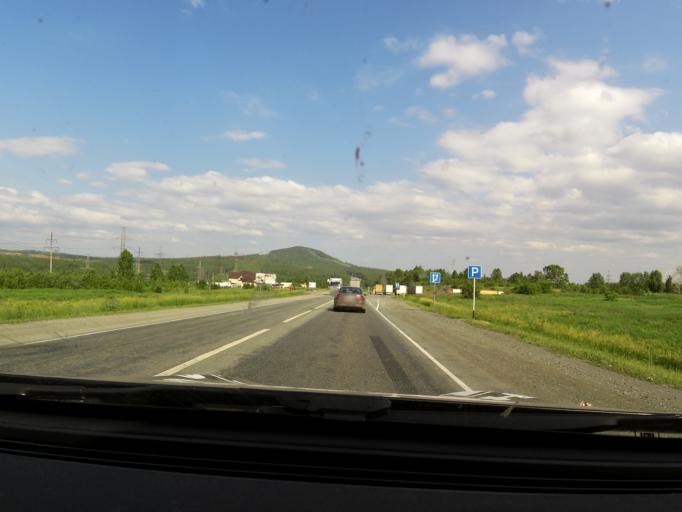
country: RU
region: Sverdlovsk
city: Revda
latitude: 56.8275
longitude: 59.9522
